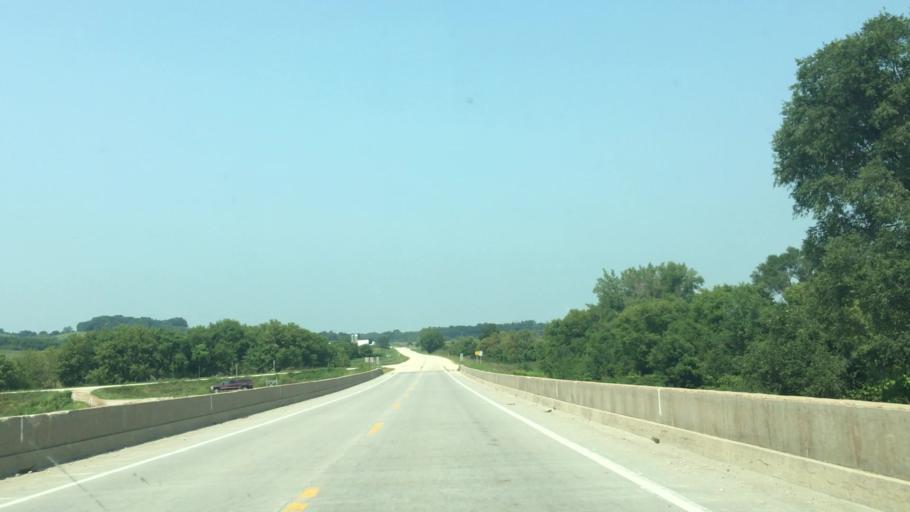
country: US
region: Iowa
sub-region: Fayette County
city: West Union
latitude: 43.0507
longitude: -91.8396
